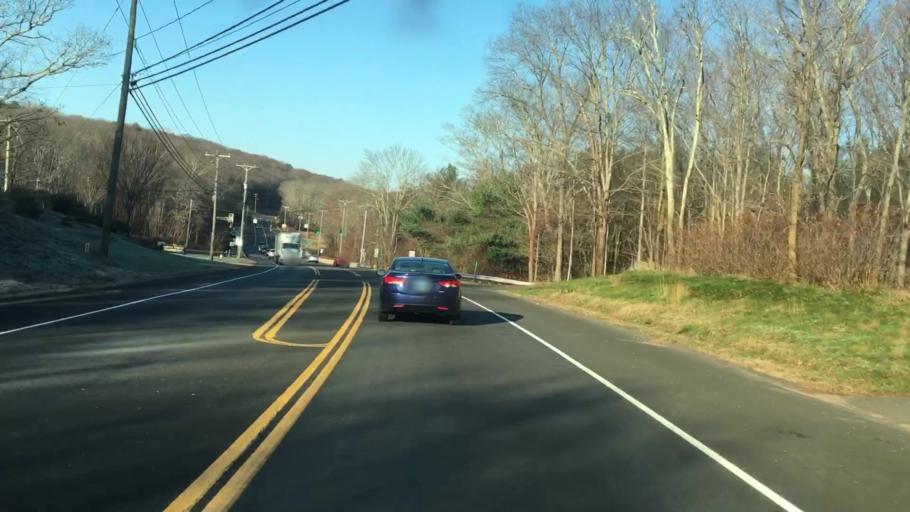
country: US
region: Connecticut
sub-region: Tolland County
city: Coventry Lake
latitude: 41.7384
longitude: -72.3667
